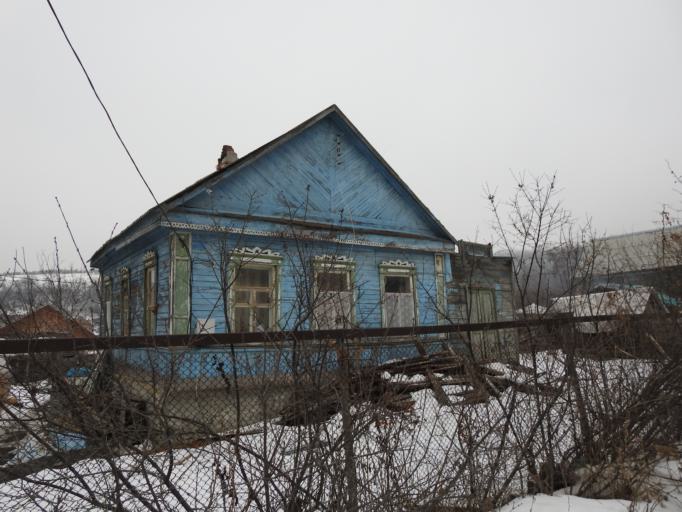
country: RU
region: Saratov
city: Sokolovyy
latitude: 51.4908
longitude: 45.8891
